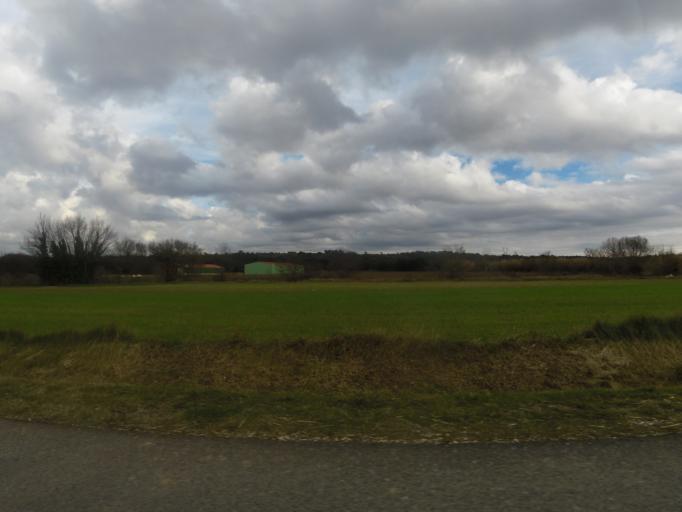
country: FR
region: Languedoc-Roussillon
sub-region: Departement du Gard
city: Saint-Mamert-du-Gard
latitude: 43.8851
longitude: 4.1949
